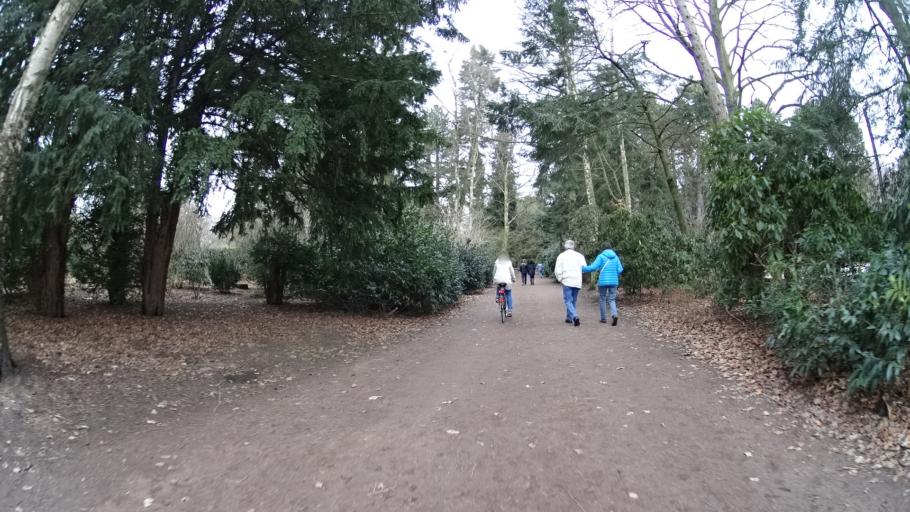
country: DE
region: Hamburg
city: Hamburg
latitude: 53.5926
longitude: 10.0161
